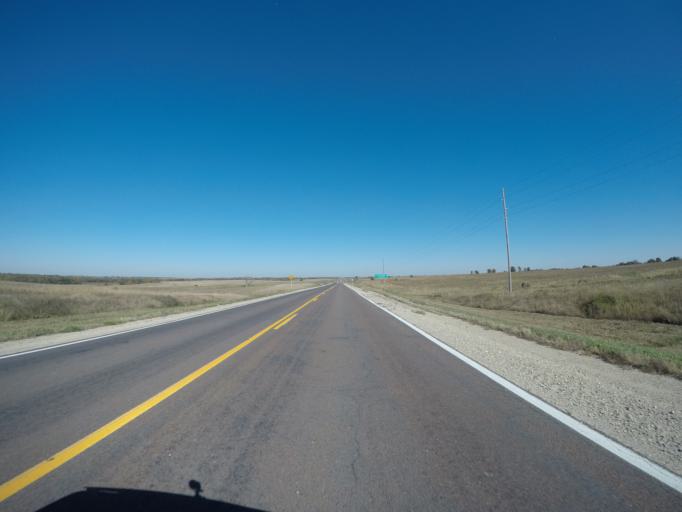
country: US
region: Kansas
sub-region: Clay County
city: Clay Center
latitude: 39.3107
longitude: -96.9236
